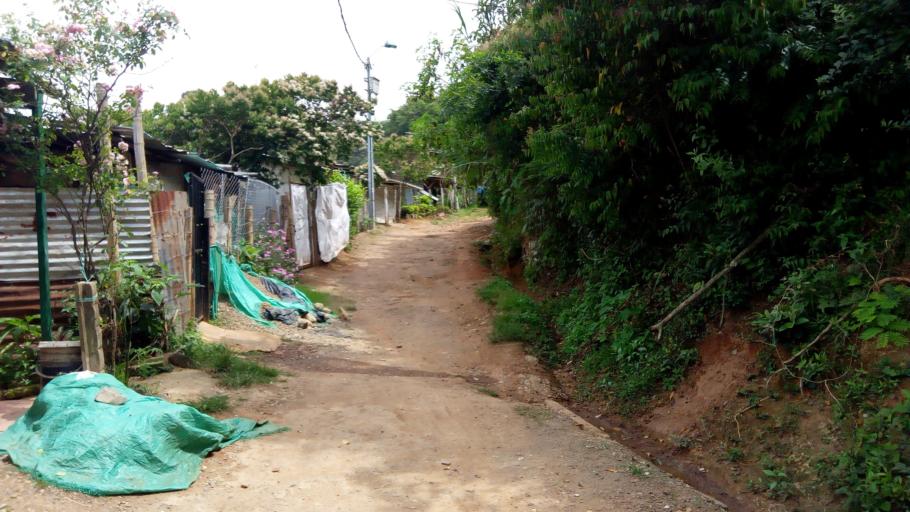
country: CO
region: Valle del Cauca
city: Cali
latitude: 3.3839
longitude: -76.5659
